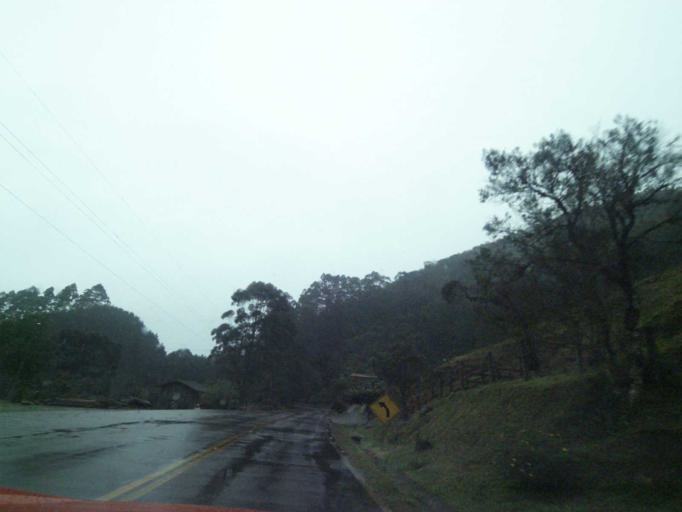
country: BR
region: Santa Catarina
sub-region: Anitapolis
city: Anitapolis
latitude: -27.7890
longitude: -49.0437
